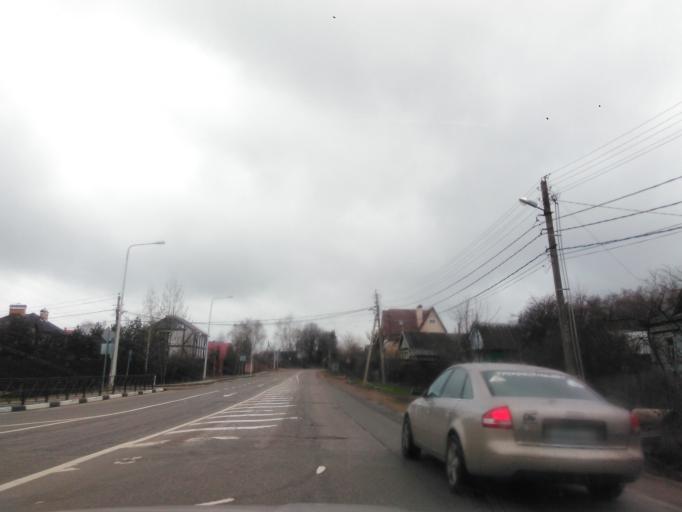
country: RU
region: Moskovskaya
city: Rozhdestveno
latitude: 55.8424
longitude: 37.0018
